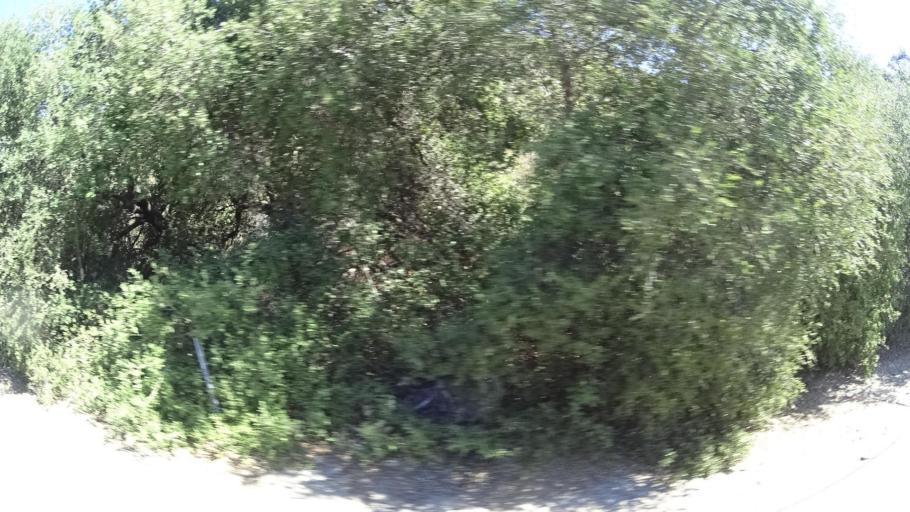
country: US
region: California
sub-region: San Diego County
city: Alpine
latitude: 32.7160
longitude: -116.7531
